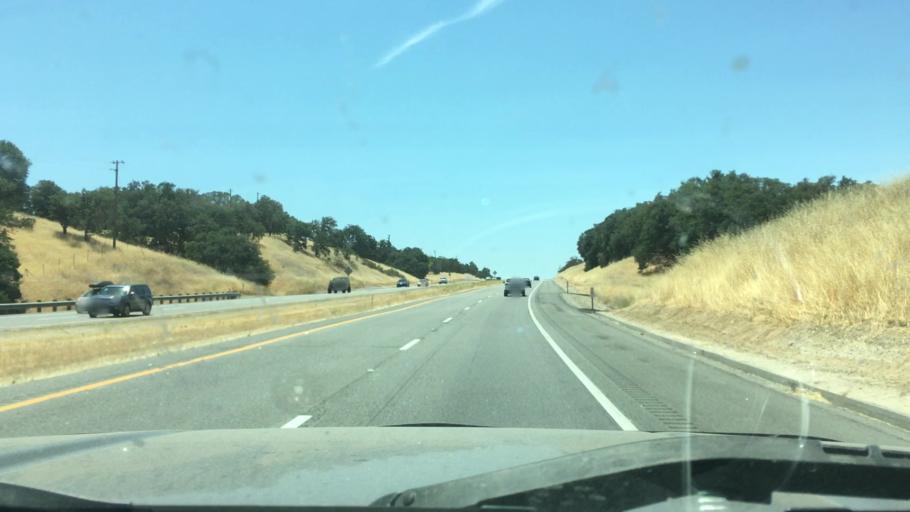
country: US
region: California
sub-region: San Luis Obispo County
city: San Miguel
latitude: 35.7109
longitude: -120.6944
